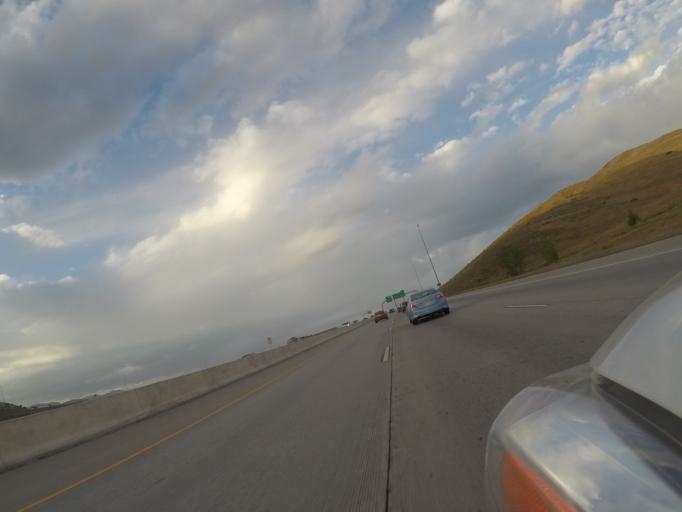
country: US
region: Colorado
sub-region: Jefferson County
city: West Pleasant View
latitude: 39.7029
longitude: -105.1935
